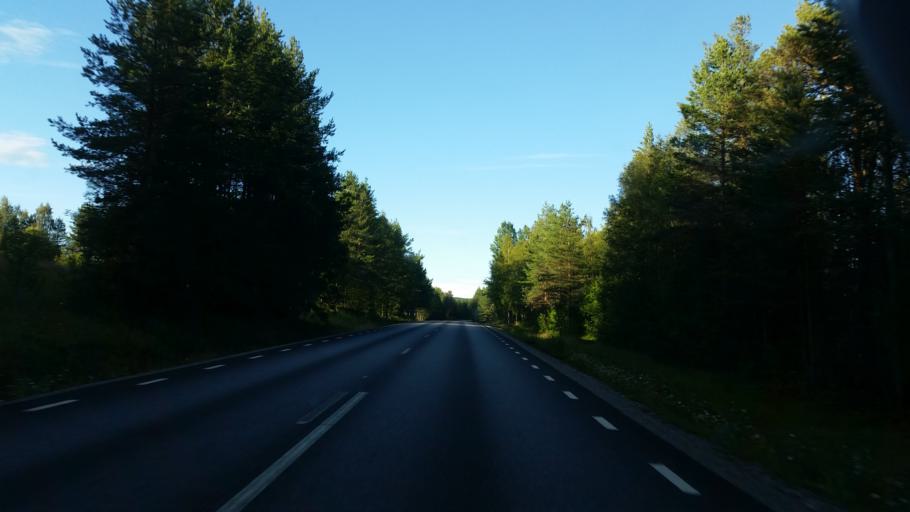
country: SE
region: Vaesterbotten
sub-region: Dorotea Kommun
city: Dorotea
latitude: 64.2429
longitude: 16.3202
